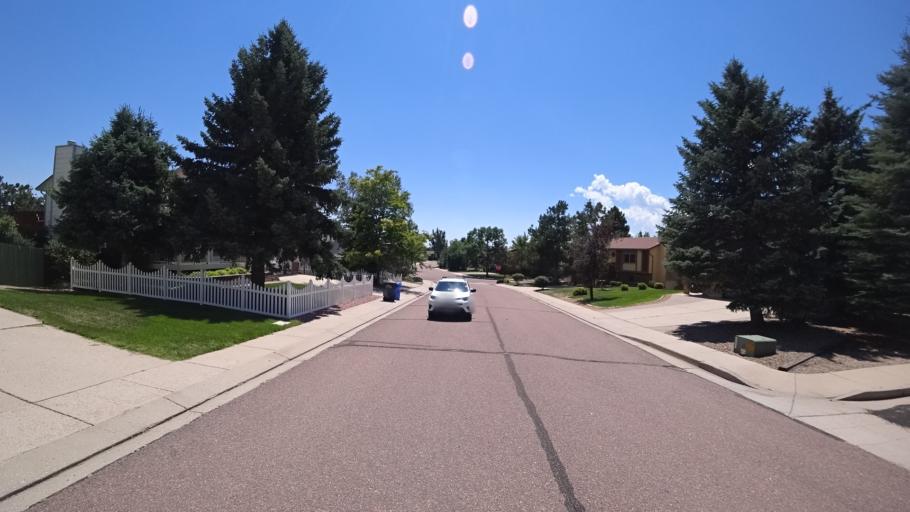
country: US
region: Colorado
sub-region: El Paso County
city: Black Forest
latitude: 38.9555
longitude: -104.7536
